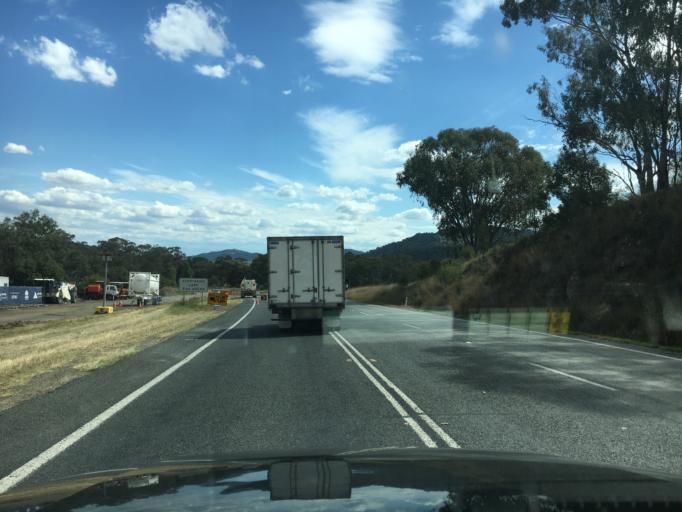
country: AU
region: New South Wales
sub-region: Liverpool Plains
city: Quirindi
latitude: -31.4506
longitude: 150.8642
